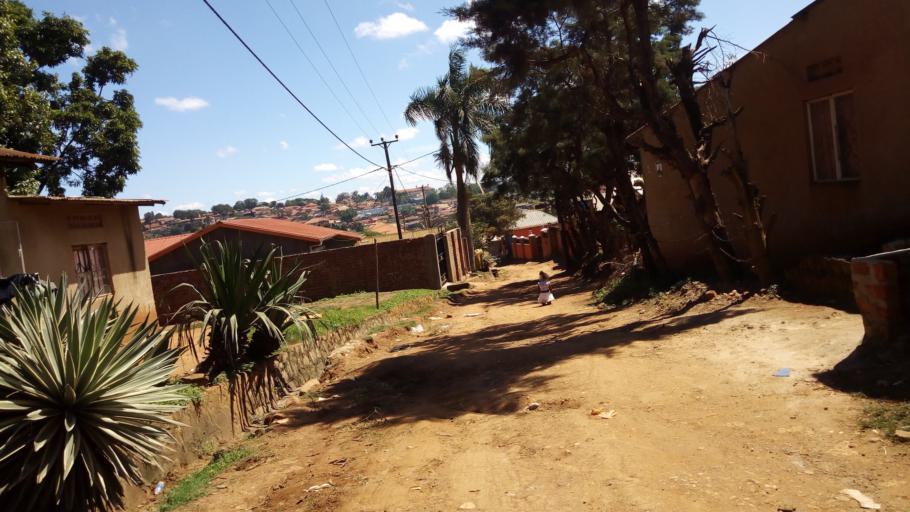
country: UG
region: Central Region
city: Kampala Central Division
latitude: 0.3577
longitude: 32.5575
